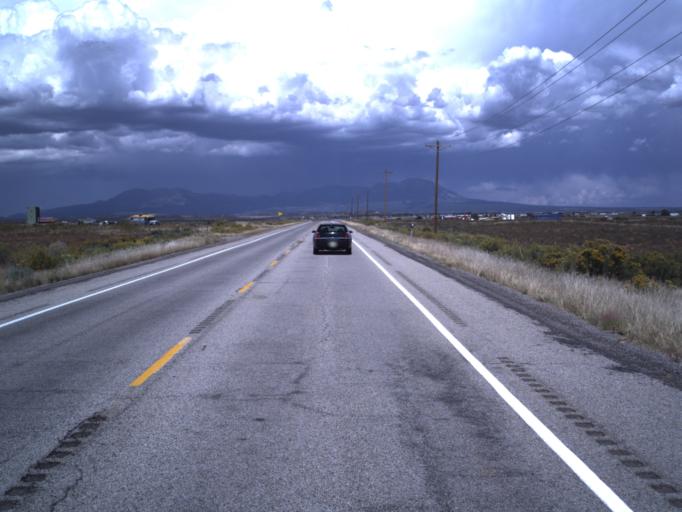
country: US
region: Utah
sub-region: San Juan County
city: Blanding
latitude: 37.5649
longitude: -109.4894
